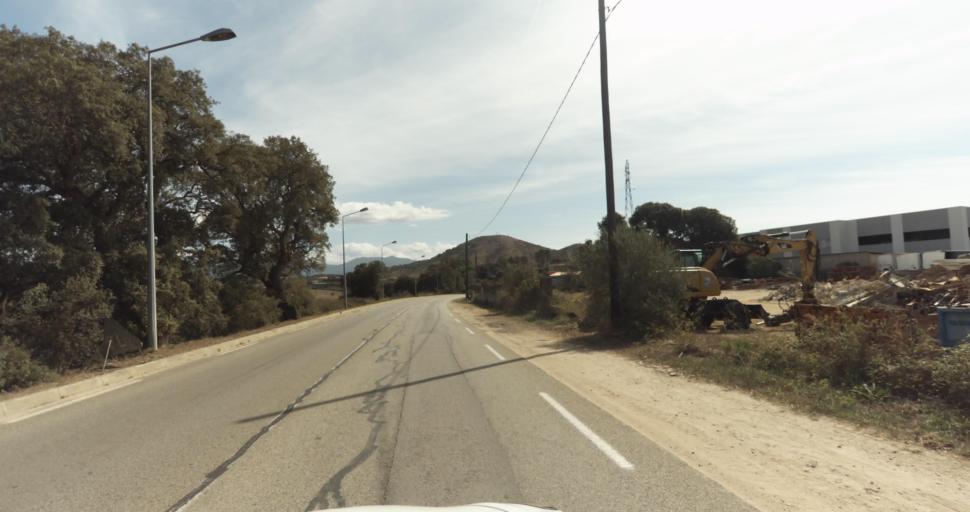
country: FR
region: Corsica
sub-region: Departement de la Corse-du-Sud
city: Afa
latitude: 41.9579
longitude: 8.7811
